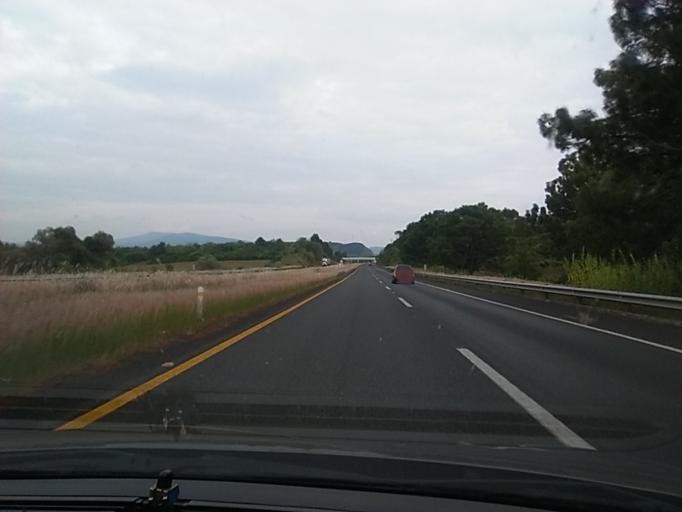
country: MX
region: Michoacan
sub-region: Puruandiro
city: San Lorenzo
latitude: 19.9536
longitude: -101.6544
